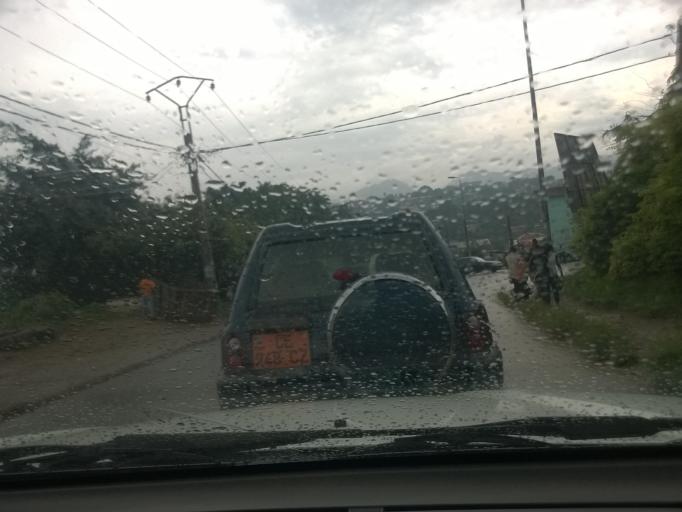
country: CM
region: Centre
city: Yaounde
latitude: 3.8713
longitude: 11.5336
